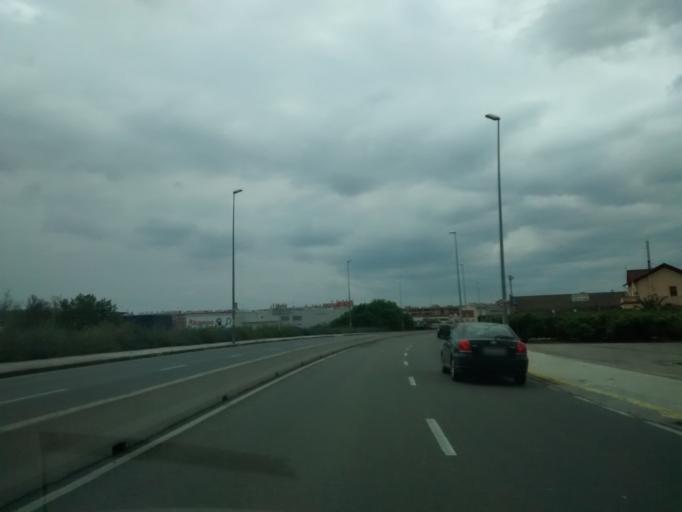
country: ES
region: Catalonia
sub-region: Provincia de Tarragona
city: Tortosa
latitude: 40.8213
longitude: 0.5135
